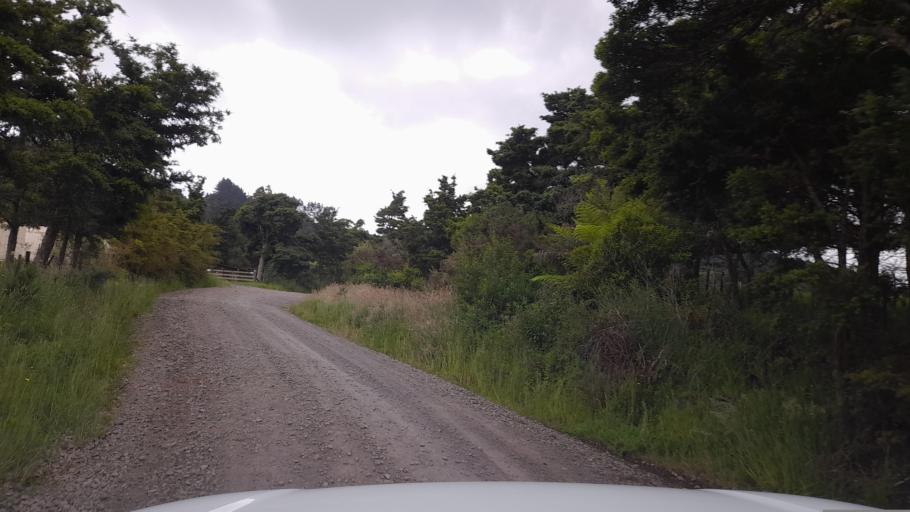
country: NZ
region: Northland
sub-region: Far North District
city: Waimate North
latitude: -35.3974
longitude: 173.7850
